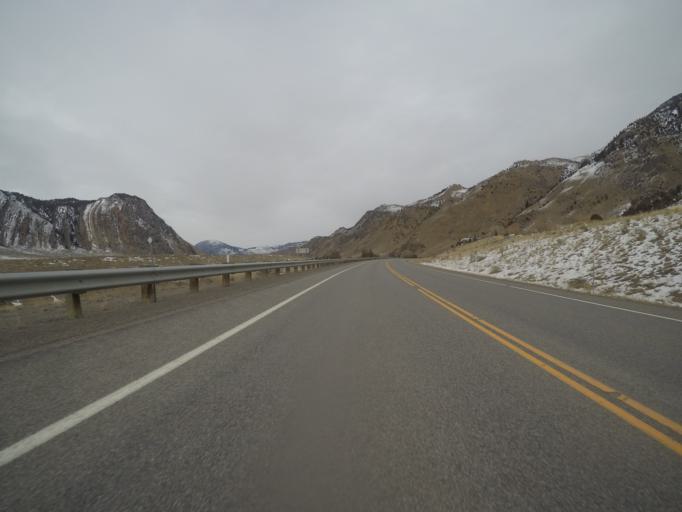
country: US
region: Montana
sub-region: Gallatin County
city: Big Sky
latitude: 45.1866
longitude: -110.8941
